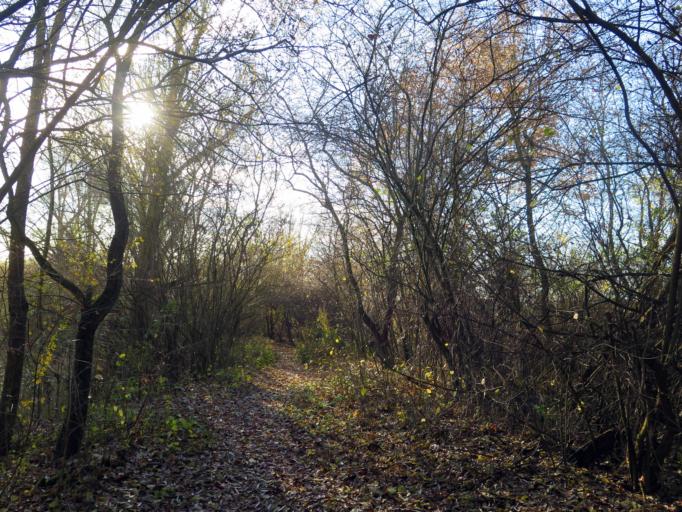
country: DE
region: Bavaria
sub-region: Regierungsbezirk Unterfranken
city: Knetzgau
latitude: 50.0039
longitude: 10.5512
